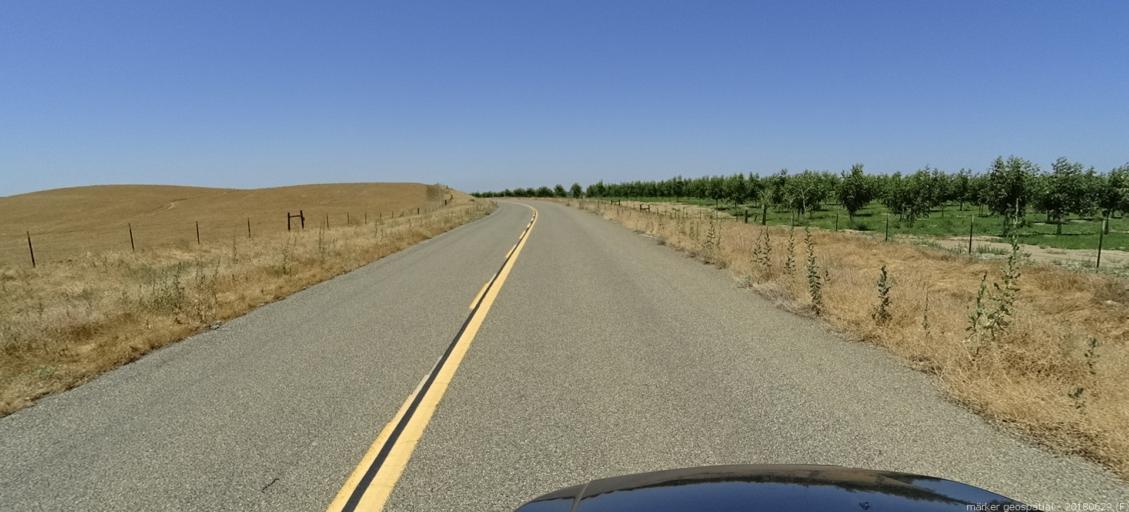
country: US
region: California
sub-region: Madera County
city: Bonadelle Ranchos-Madera Ranchos
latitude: 37.0384
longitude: -119.9338
